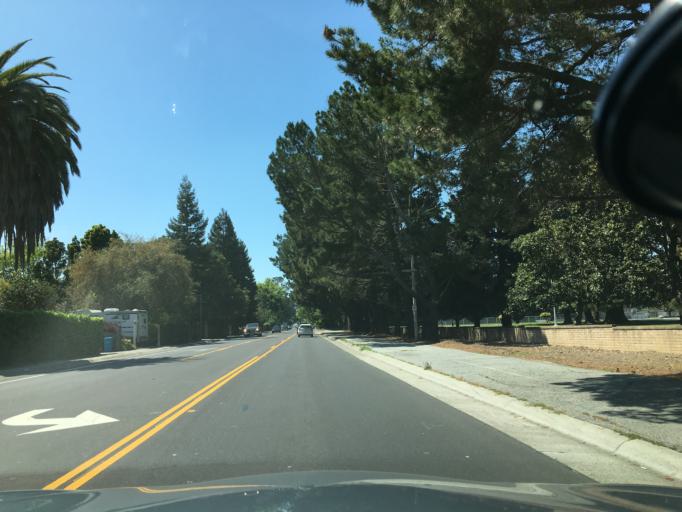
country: US
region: California
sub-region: San Mateo County
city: Belmont
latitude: 37.5147
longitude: -122.2853
